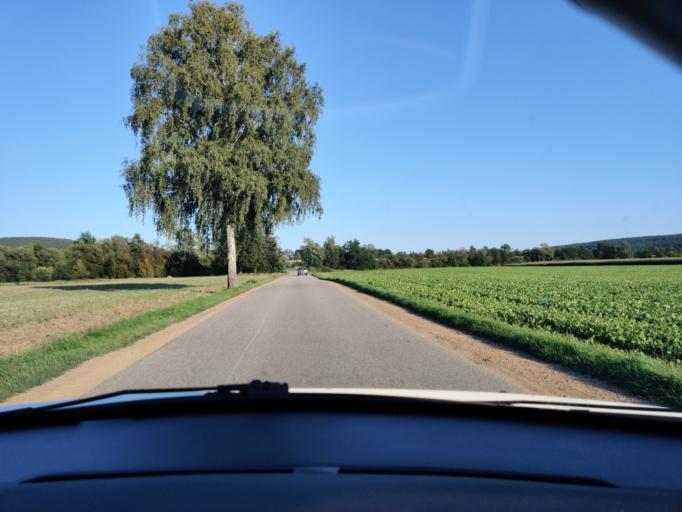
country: DE
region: Bavaria
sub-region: Upper Palatinate
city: Stulln
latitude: 49.4095
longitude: 12.1596
